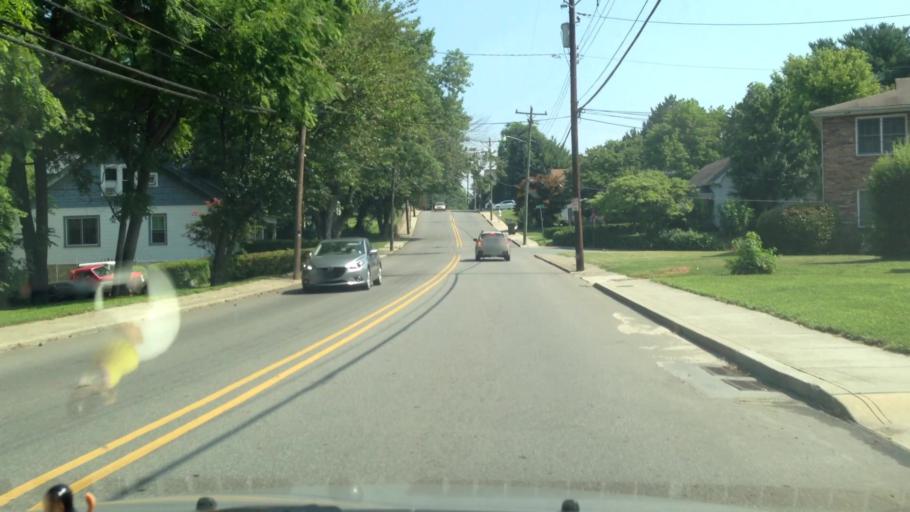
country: US
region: North Carolina
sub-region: Surry County
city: Mount Airy
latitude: 36.4936
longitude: -80.6100
